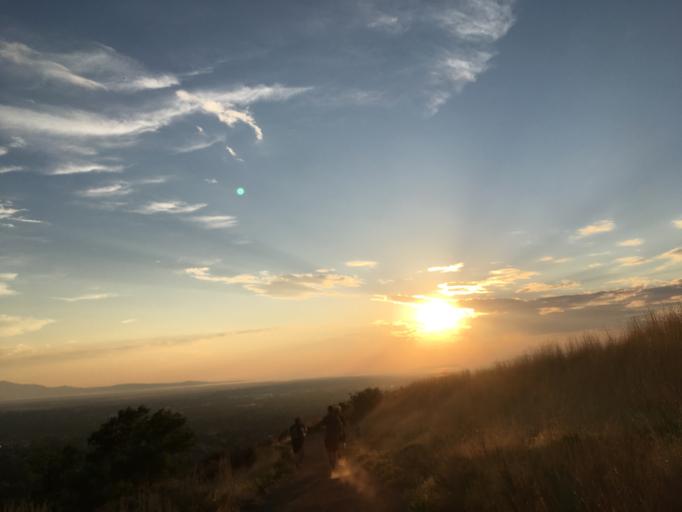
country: US
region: Utah
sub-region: Davis County
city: Fruit Heights
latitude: 41.0664
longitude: -111.9043
